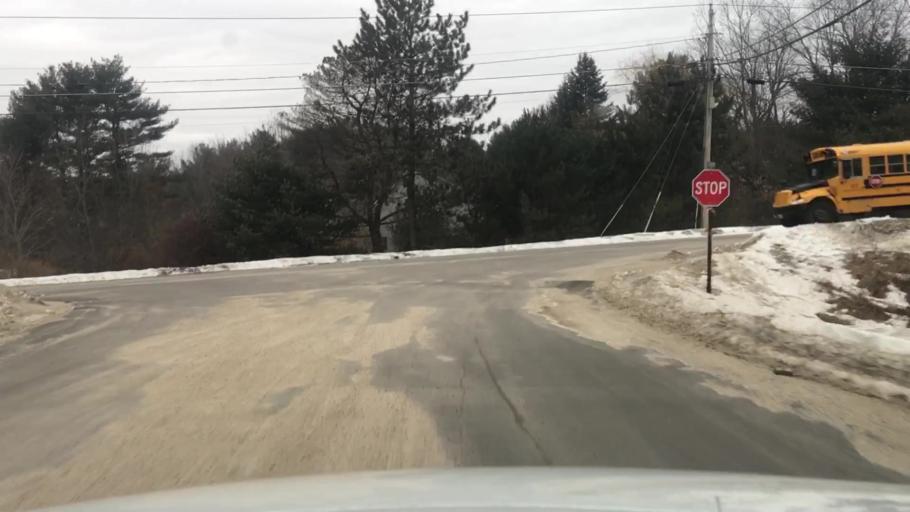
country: US
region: Maine
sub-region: York County
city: Shapleigh
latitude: 43.5289
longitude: -70.8496
